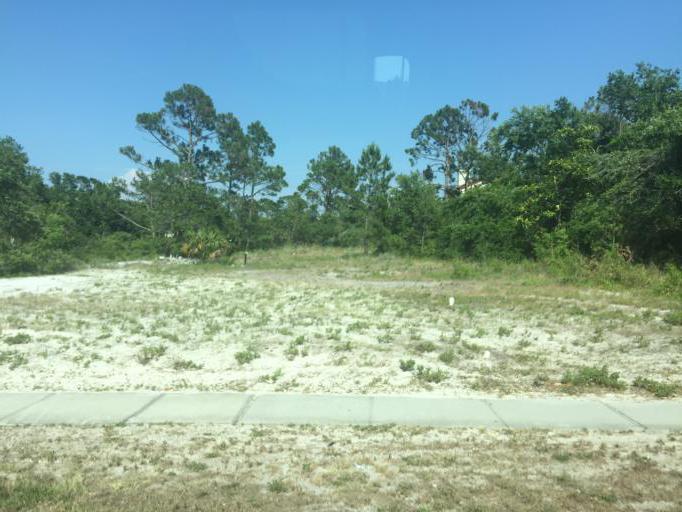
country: US
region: Florida
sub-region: Bay County
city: Panama City Beach
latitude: 30.1699
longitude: -85.7898
